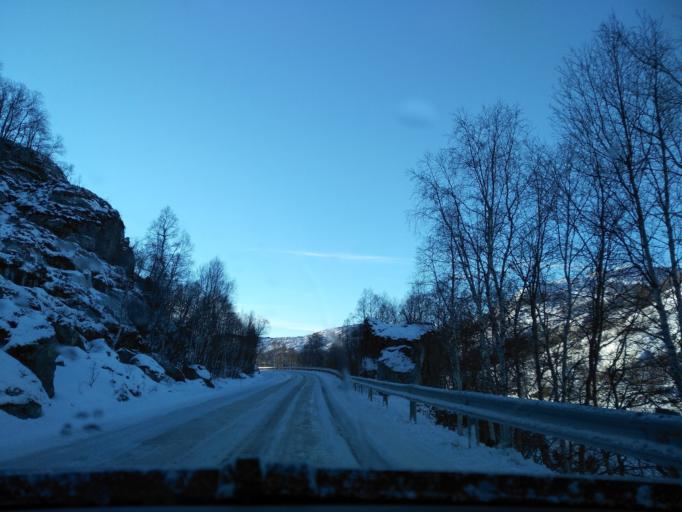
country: NO
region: Vest-Agder
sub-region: Sirdal
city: Tonstad
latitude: 59.0100
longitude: 6.9346
